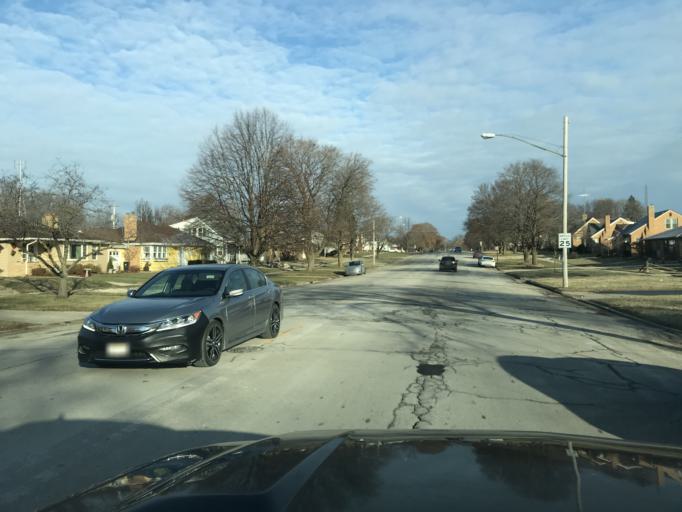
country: US
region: Wisconsin
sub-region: Kenosha County
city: Kenosha
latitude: 42.5667
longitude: -87.8588
